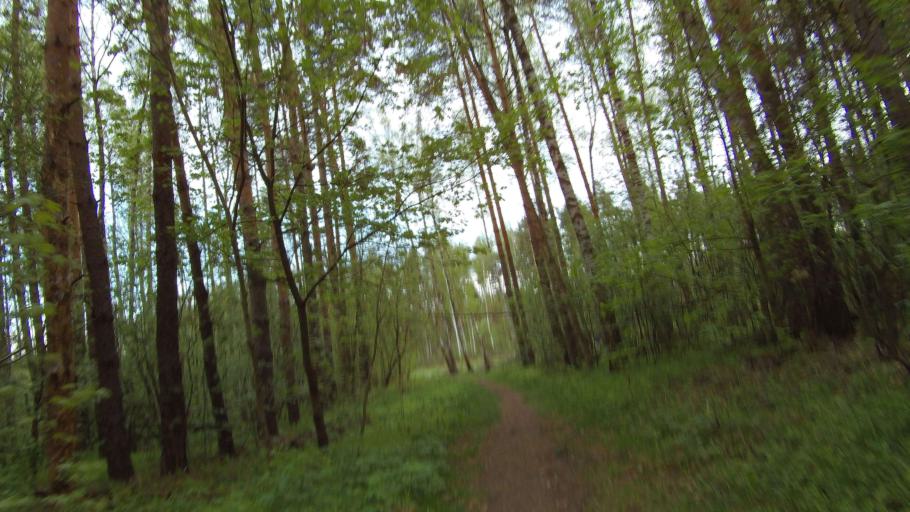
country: RU
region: Moskovskaya
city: Ramenskoye
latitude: 55.5866
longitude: 38.2234
